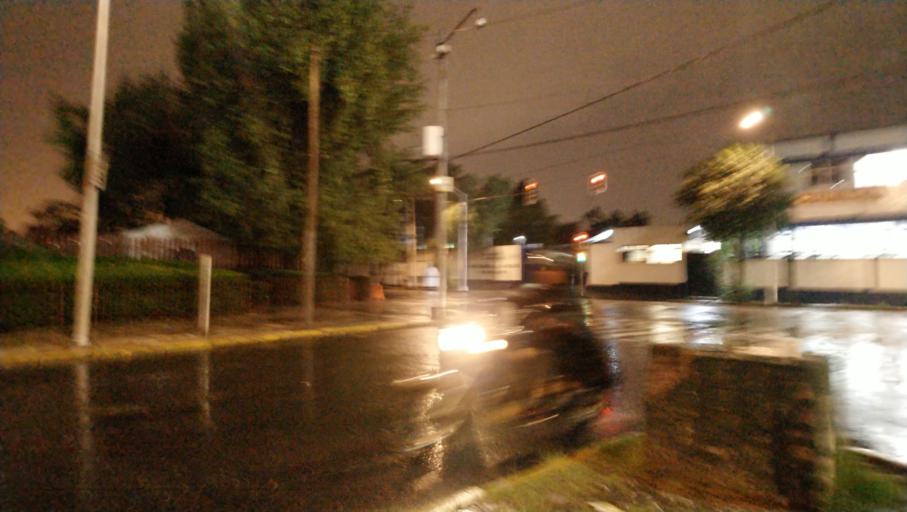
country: MX
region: Mexico City
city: Mexico City
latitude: 19.4275
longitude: -99.1160
